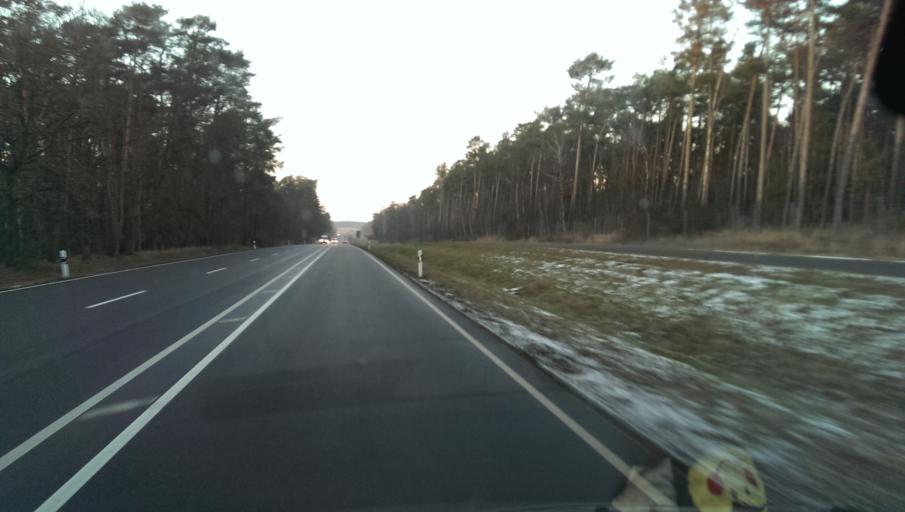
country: DE
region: Brandenburg
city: Herzberg
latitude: 51.6523
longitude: 13.2919
